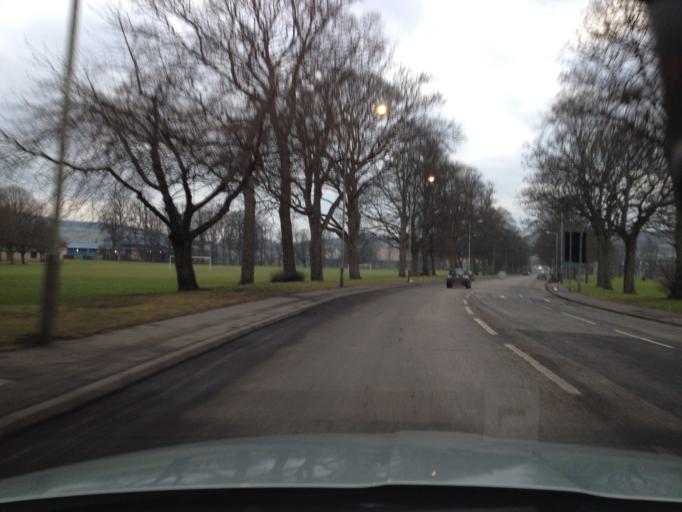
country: GB
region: Scotland
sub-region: Perth and Kinross
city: Perth
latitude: 56.3912
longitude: -3.4286
